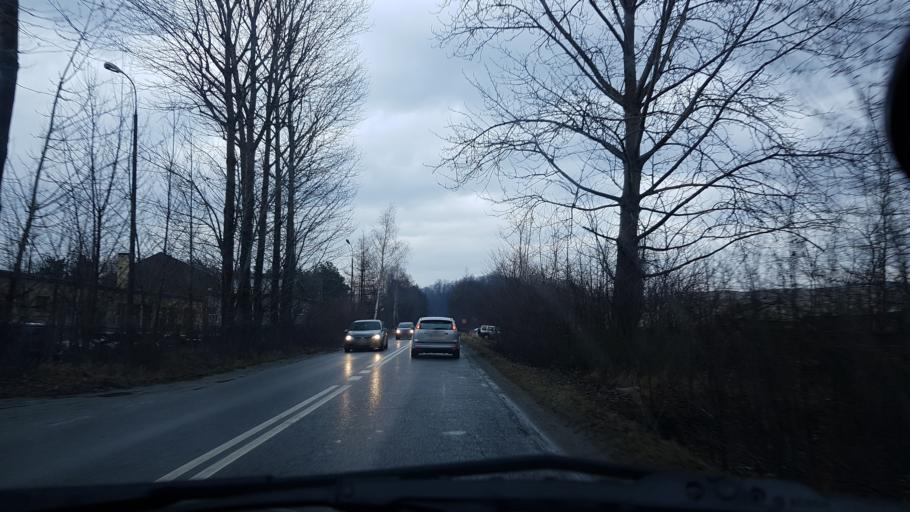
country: PL
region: Silesian Voivodeship
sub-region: Powiat zywiecki
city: Lekawica
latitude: 49.7114
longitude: 19.2532
